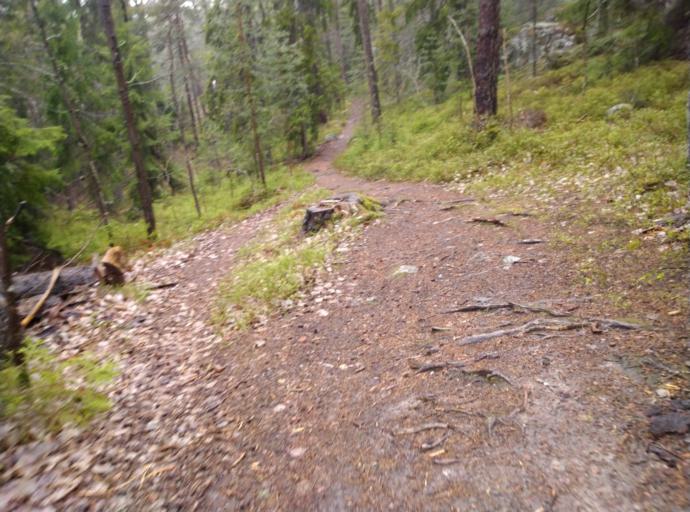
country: SE
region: Stockholm
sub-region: Nacka Kommun
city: Fisksatra
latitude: 59.2937
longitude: 18.2699
